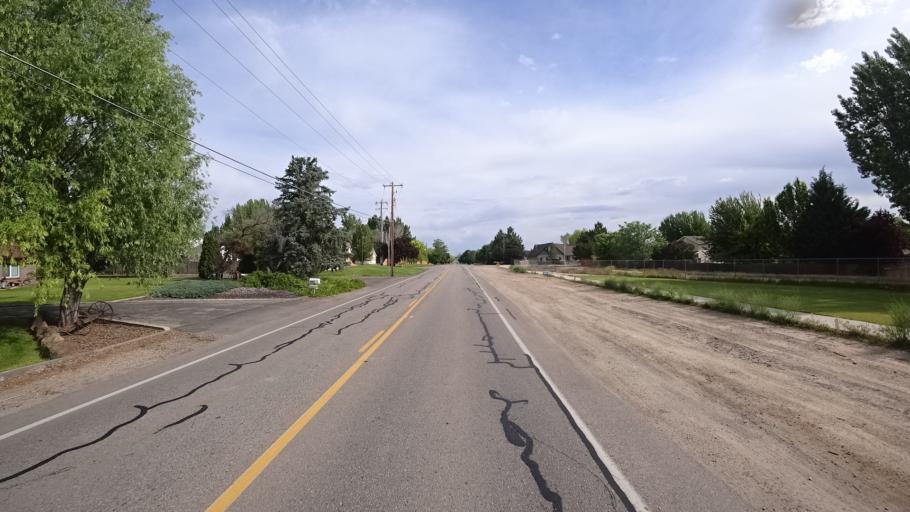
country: US
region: Idaho
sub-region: Ada County
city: Meridian
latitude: 43.5780
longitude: -116.3746
